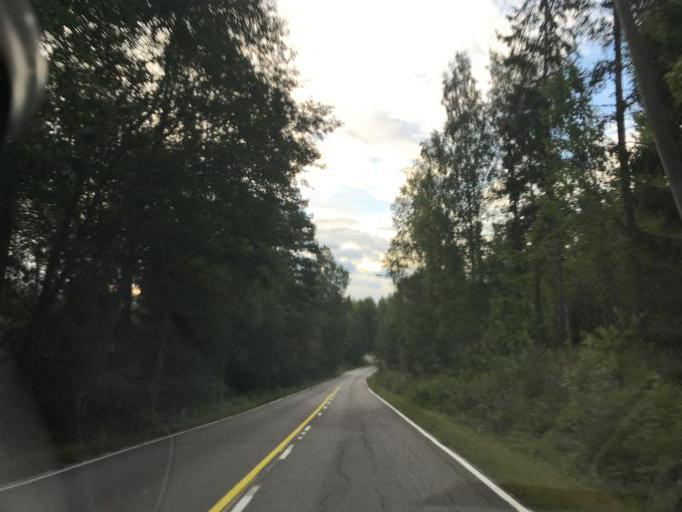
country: FI
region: Uusimaa
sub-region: Helsinki
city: Vihti
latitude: 60.4095
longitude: 24.4769
